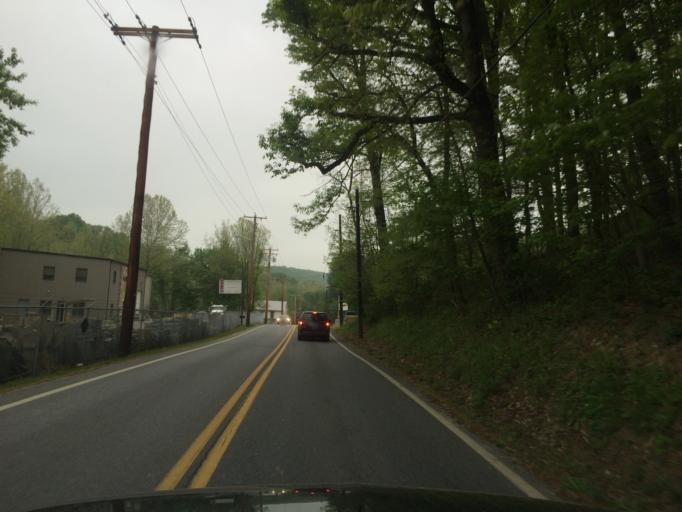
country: US
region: Maryland
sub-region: Carroll County
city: Sykesville
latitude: 39.3482
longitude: -76.9006
